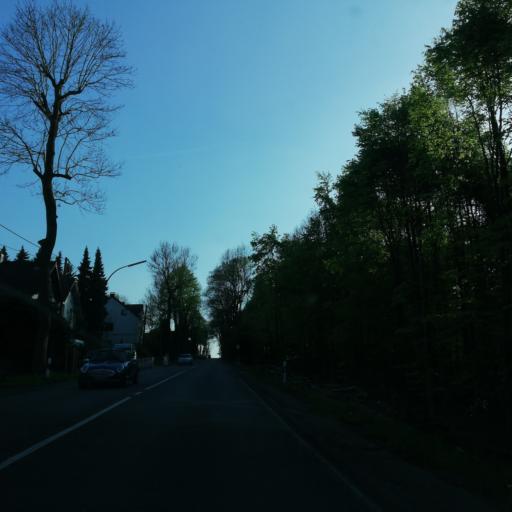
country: DE
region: North Rhine-Westphalia
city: Herdecke
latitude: 51.4386
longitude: 7.4506
